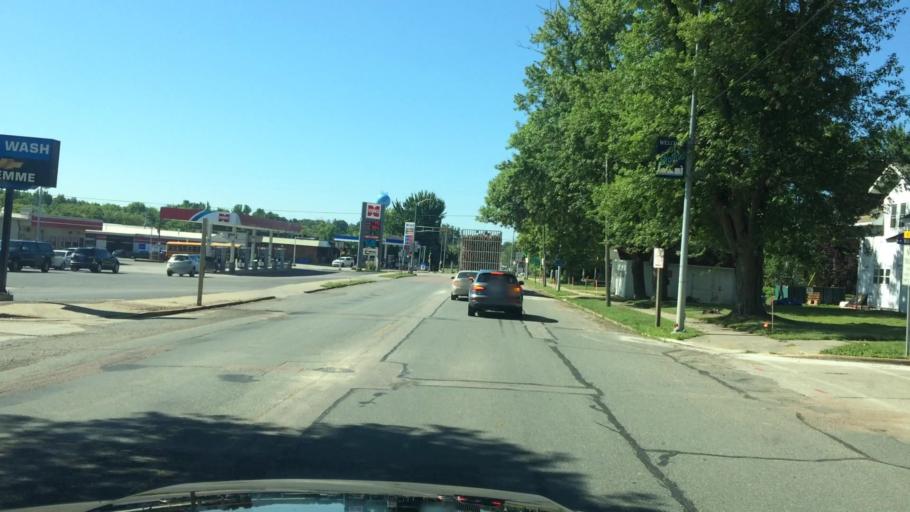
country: US
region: Wisconsin
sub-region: Marathon County
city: Stratford
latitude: 44.8021
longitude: -90.0792
